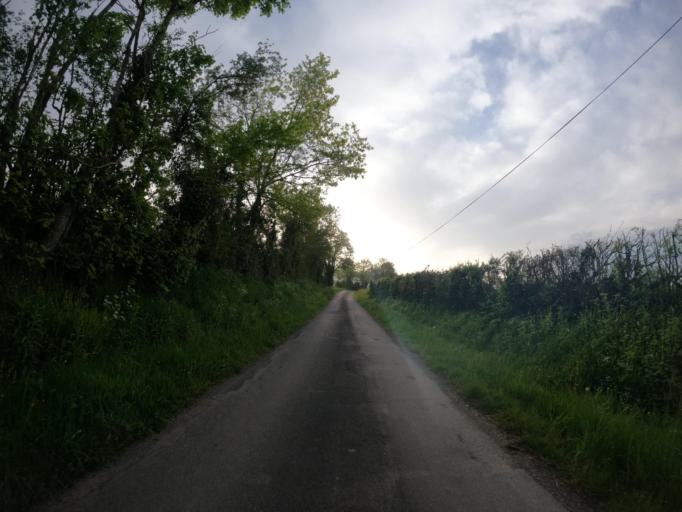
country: FR
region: Poitou-Charentes
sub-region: Departement des Deux-Sevres
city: Moncoutant
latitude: 46.7272
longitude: -0.5715
